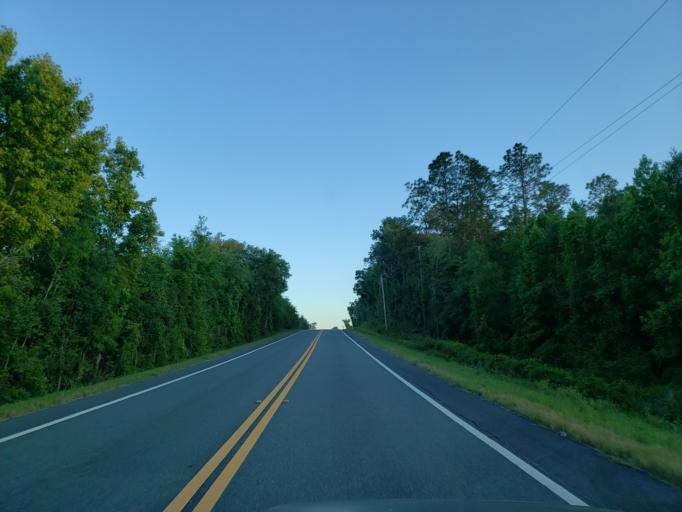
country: US
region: Florida
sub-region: Madison County
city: Madison
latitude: 30.5879
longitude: -83.2414
